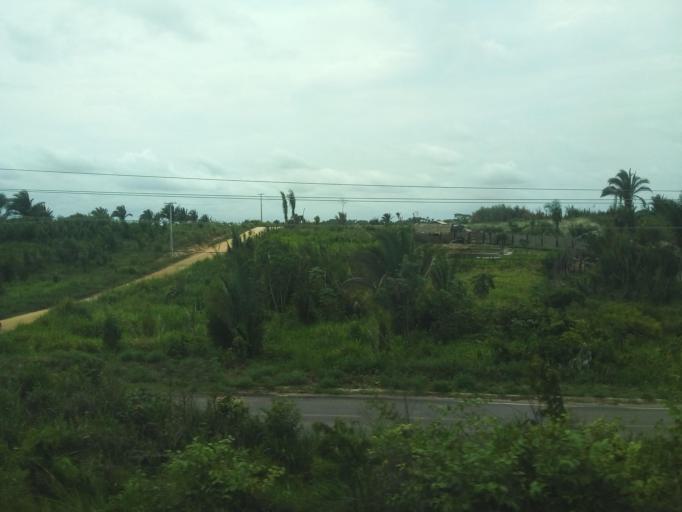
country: BR
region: Maranhao
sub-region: Santa Ines
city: Santa Ines
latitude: -3.6752
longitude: -45.8761
